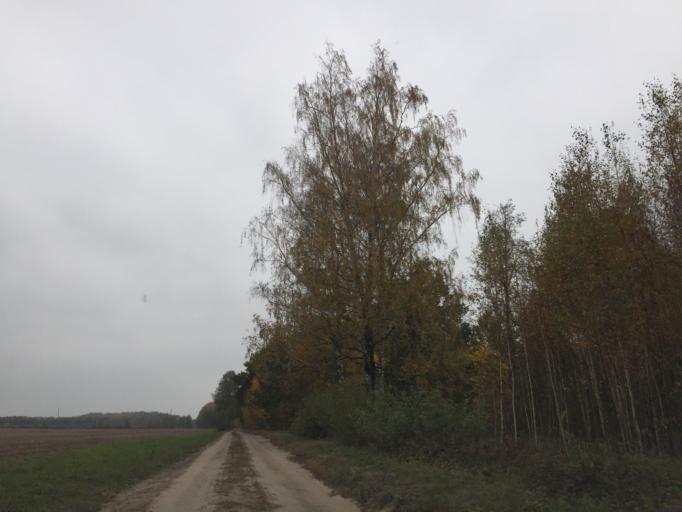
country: LV
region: Dobeles Rajons
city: Dobele
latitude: 56.6710
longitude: 23.4733
